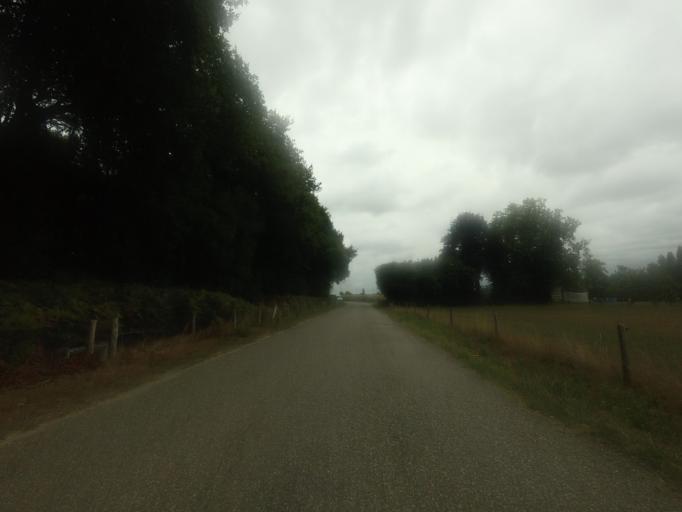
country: NL
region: Gelderland
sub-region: Gemeente Wijchen
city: Wijchen
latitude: 51.7932
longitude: 5.7565
